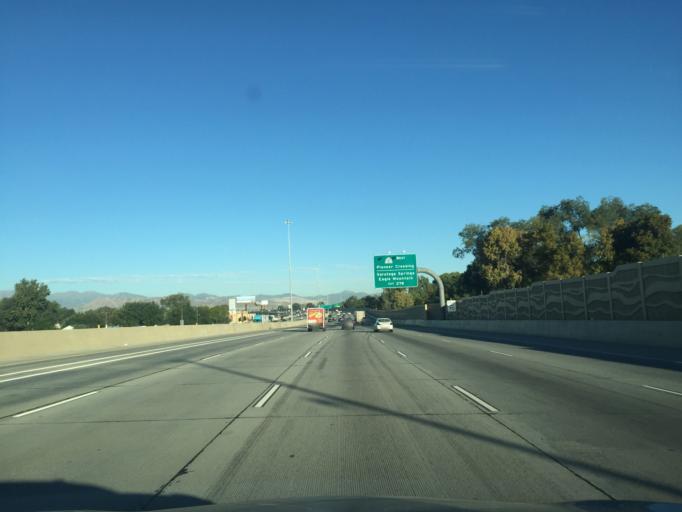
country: US
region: Utah
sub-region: Utah County
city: American Fork
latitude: 40.3677
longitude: -111.7963
